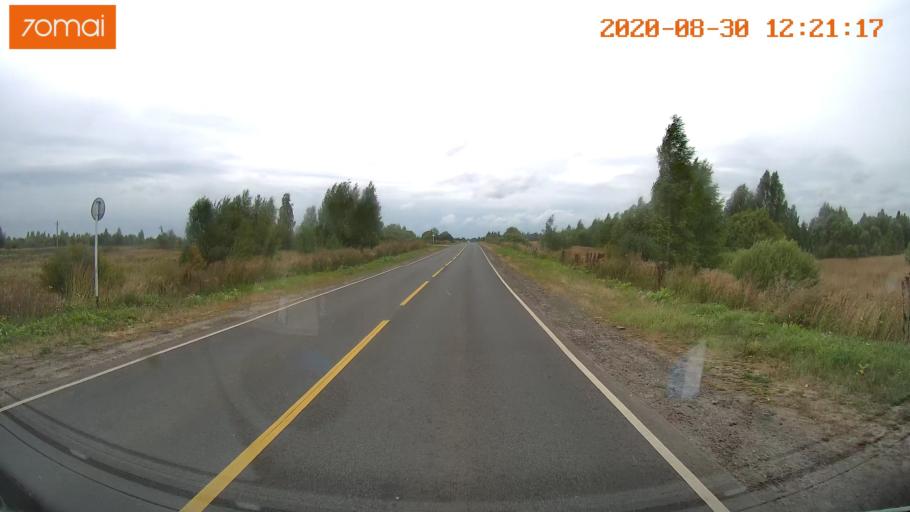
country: RU
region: Ivanovo
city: Yur'yevets
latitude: 57.3245
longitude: 42.8793
